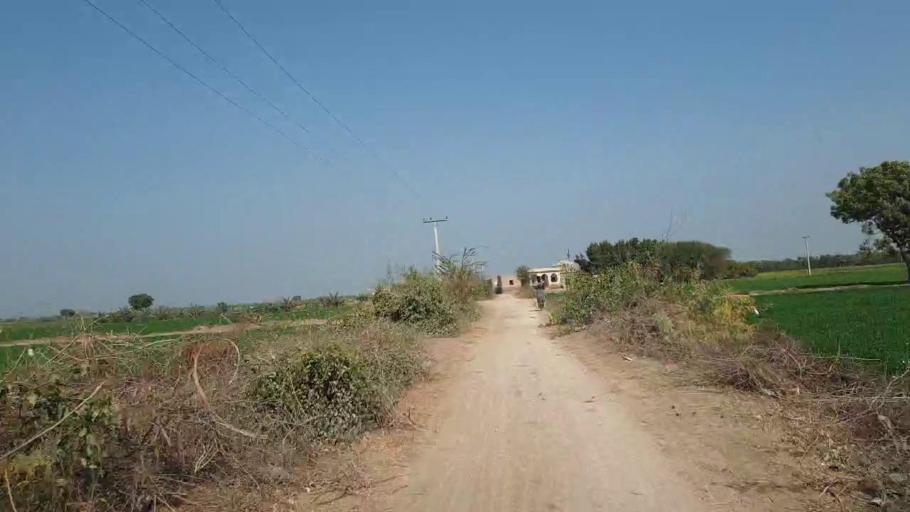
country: PK
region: Sindh
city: Hala
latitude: 25.9192
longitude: 68.4298
